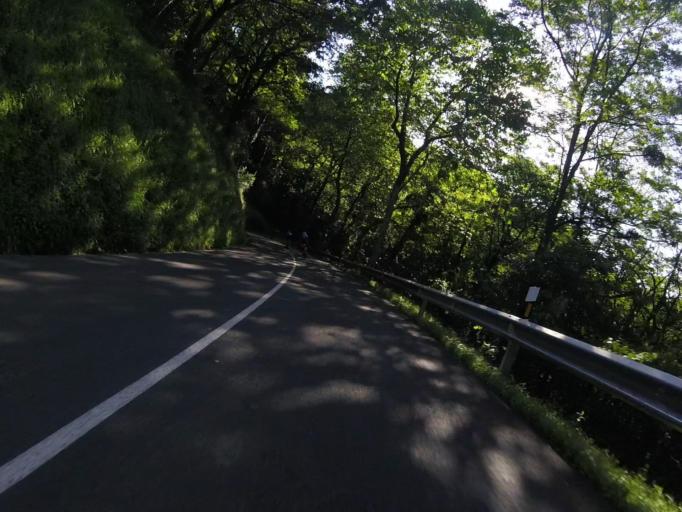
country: ES
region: Basque Country
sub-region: Provincia de Guipuzcoa
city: Asteasu
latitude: 43.2043
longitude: -2.1104
